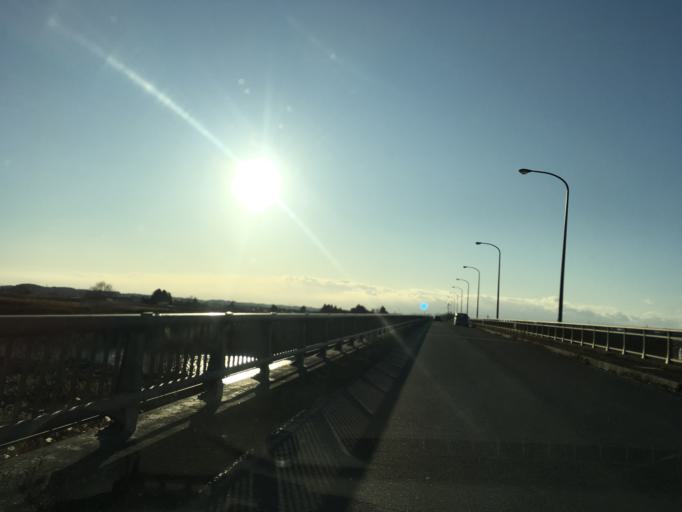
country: JP
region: Iwate
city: Ichinoseki
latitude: 38.7452
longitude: 141.1539
